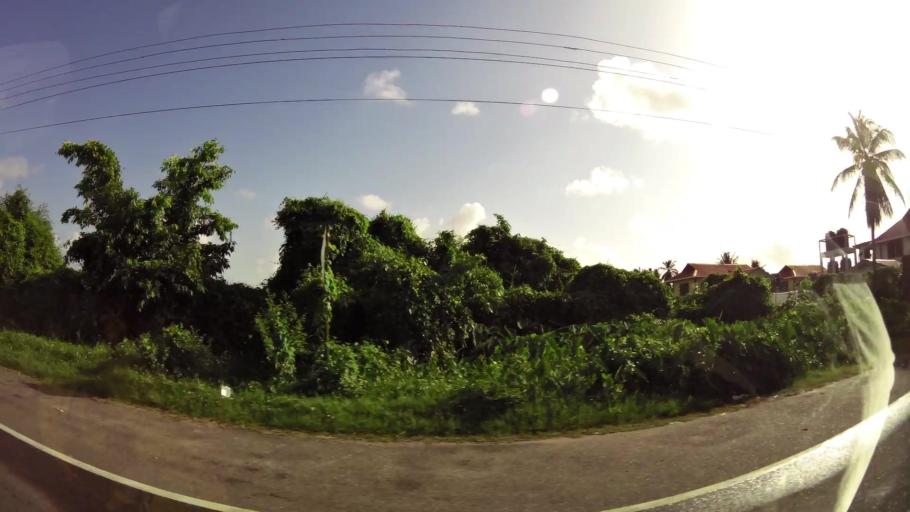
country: GY
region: Demerara-Mahaica
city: Georgetown
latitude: 6.8202
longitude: -58.0931
